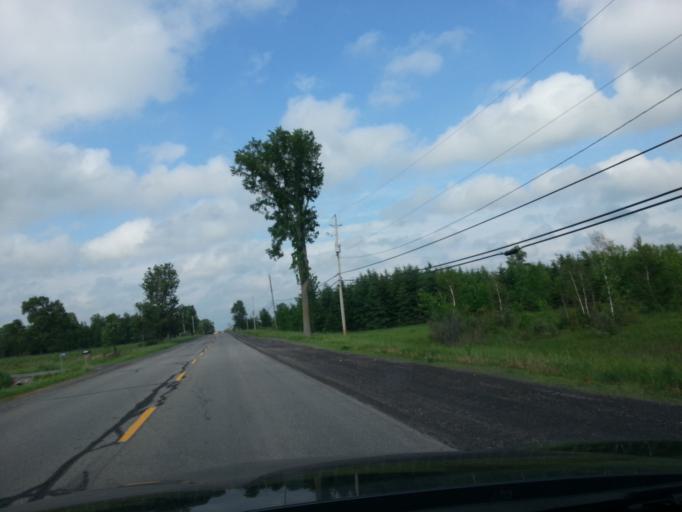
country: CA
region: Ontario
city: Bells Corners
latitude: 45.1545
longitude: -75.9012
